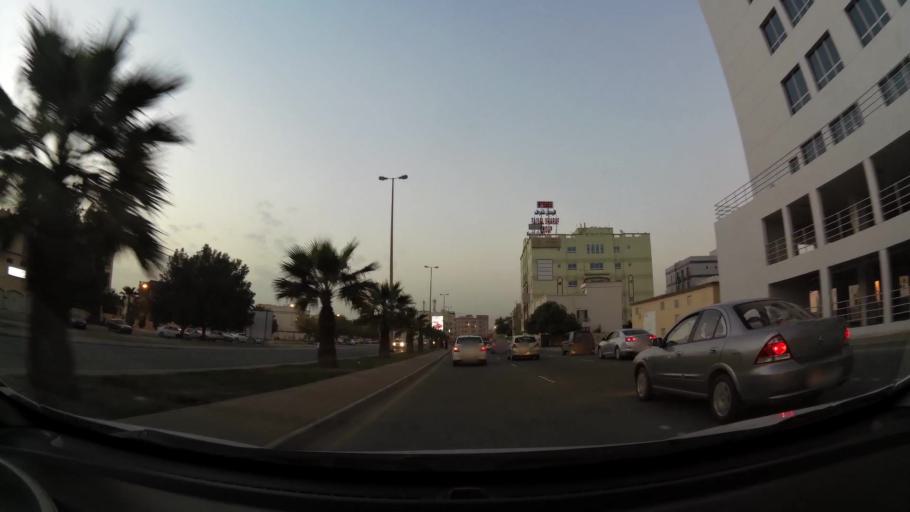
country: BH
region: Manama
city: Manama
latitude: 26.2095
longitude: 50.5667
